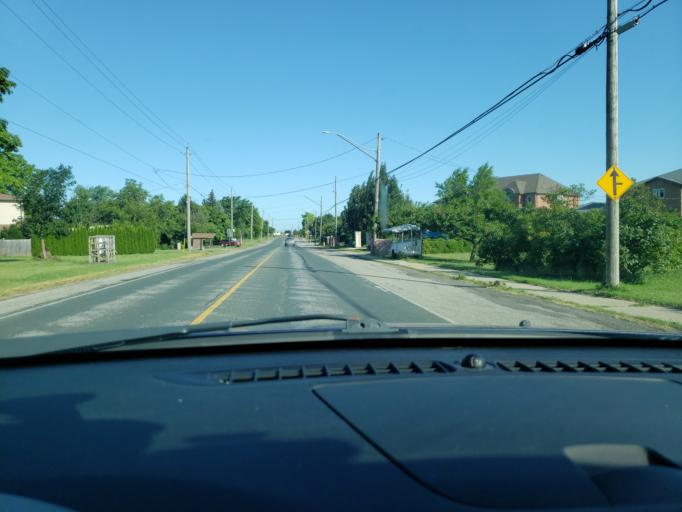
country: CA
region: Ontario
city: Hamilton
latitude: 43.1979
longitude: -79.6061
